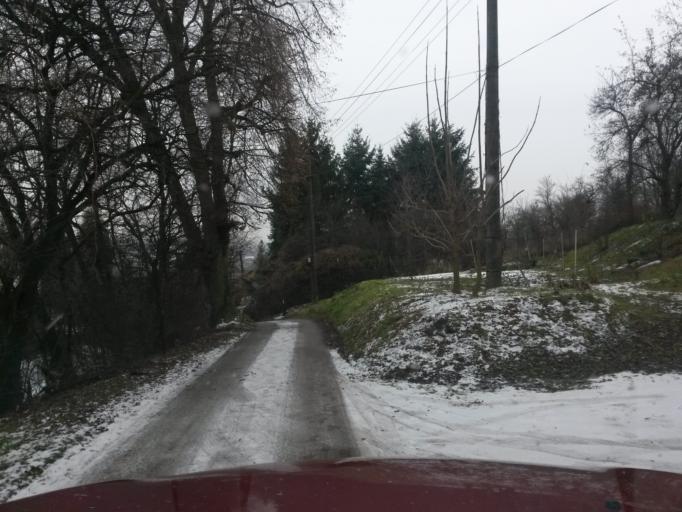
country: SK
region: Kosicky
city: Kosice
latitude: 48.7151
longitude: 21.2830
